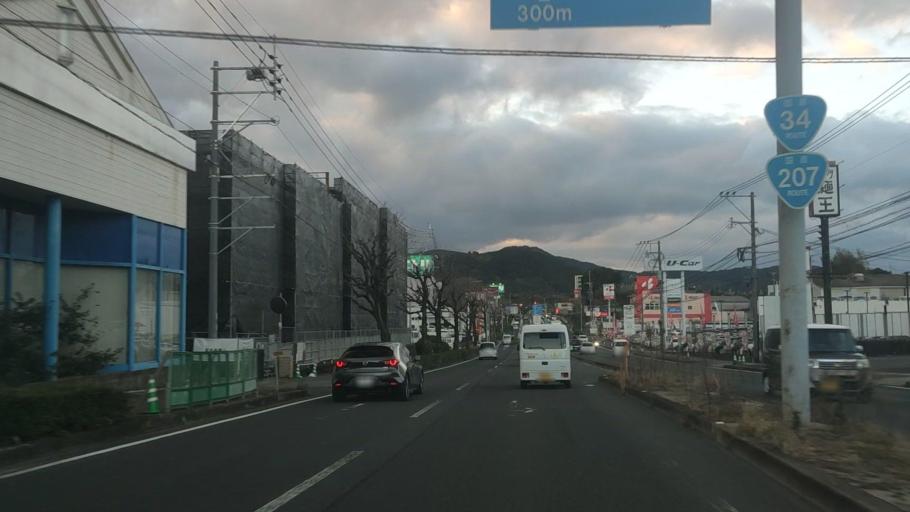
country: JP
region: Nagasaki
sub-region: Isahaya-shi
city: Isahaya
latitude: 32.8293
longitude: 129.9942
